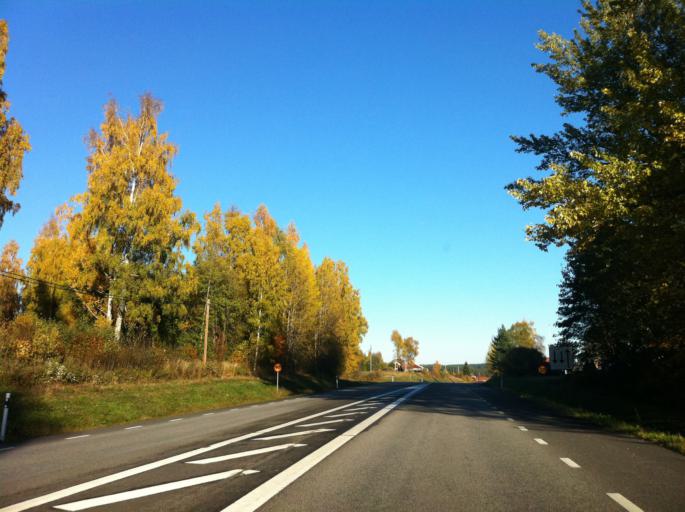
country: SE
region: Dalarna
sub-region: Rattviks Kommun
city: Vikarbyn
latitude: 60.9098
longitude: 15.0090
